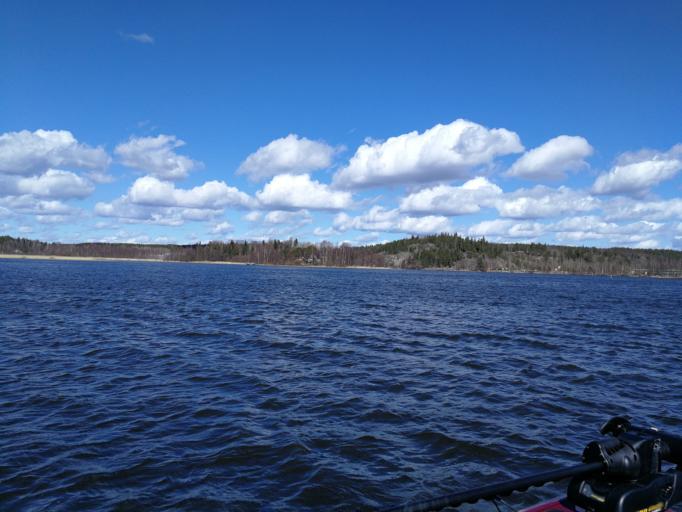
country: FI
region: Uusimaa
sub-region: Raaseporin
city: Pohja
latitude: 60.0883
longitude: 23.5474
